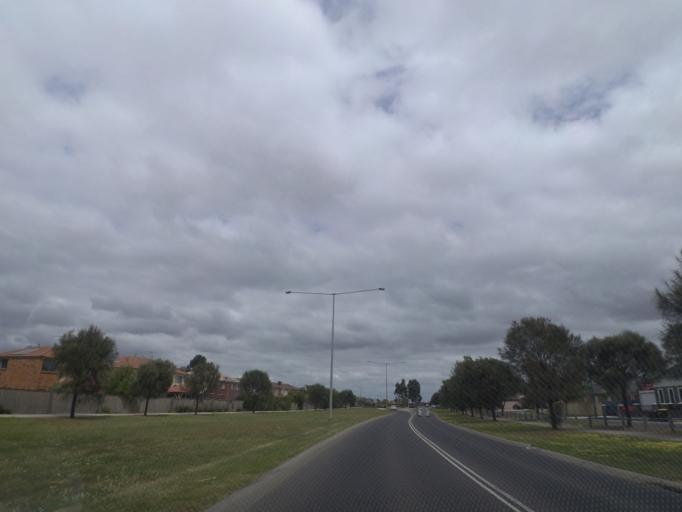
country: AU
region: Victoria
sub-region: Melton
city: Taylors Hill
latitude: -37.7145
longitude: 144.7553
